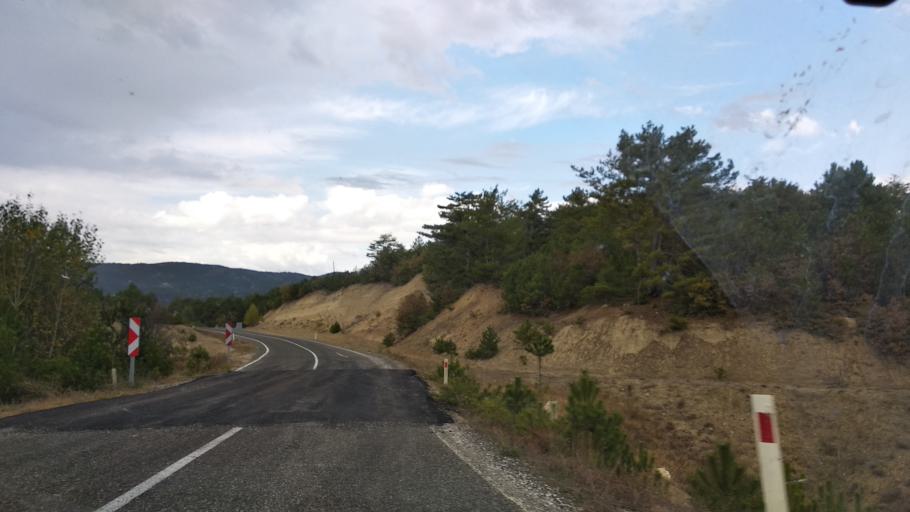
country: TR
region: Bolu
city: Seben
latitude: 40.3364
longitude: 31.4373
